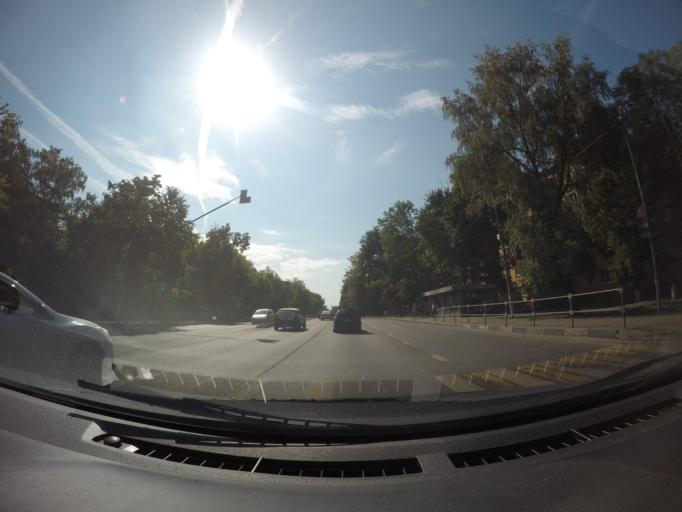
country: RU
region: Moskovskaya
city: Lyubertsy
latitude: 55.6661
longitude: 37.9090
